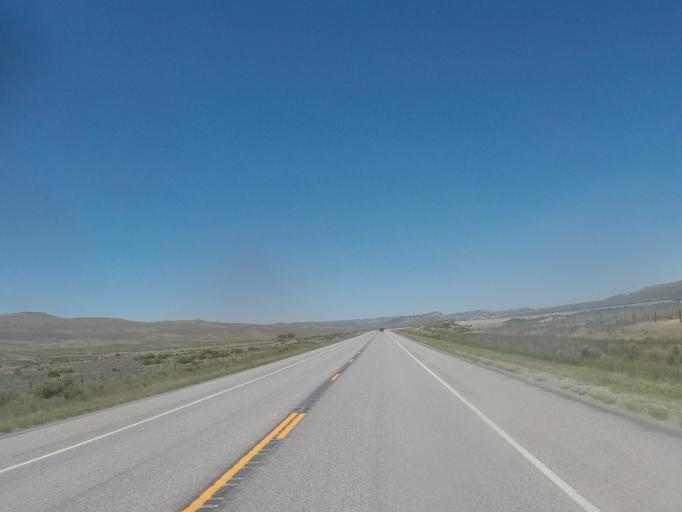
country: US
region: Montana
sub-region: Carbon County
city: Red Lodge
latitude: 45.1657
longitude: -108.8300
